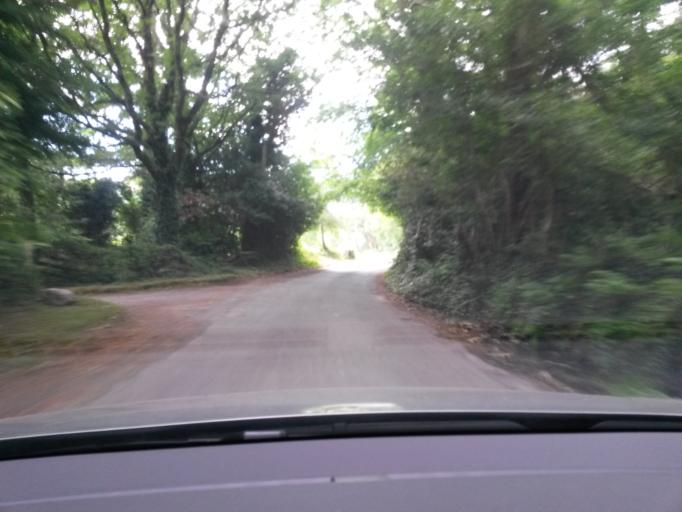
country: IE
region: Leinster
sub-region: Wicklow
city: Enniskerry
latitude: 53.1594
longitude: -6.2018
